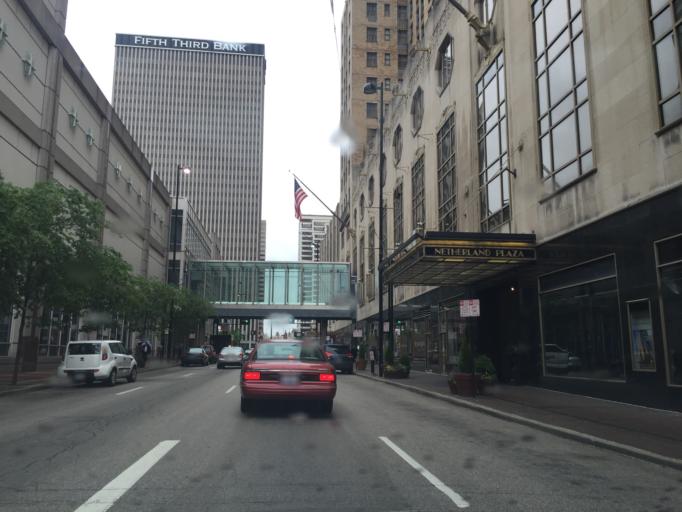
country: US
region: Kentucky
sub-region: Kenton County
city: Covington
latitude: 39.1009
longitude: -84.5145
